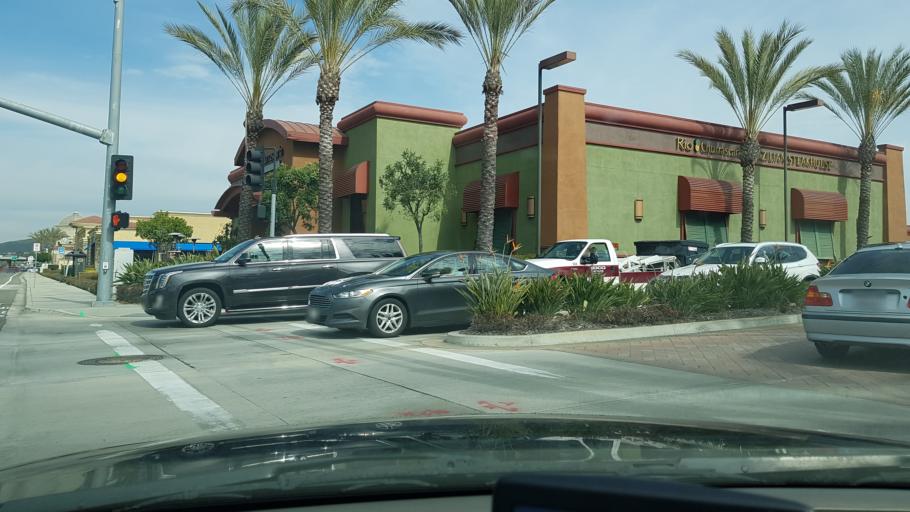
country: US
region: California
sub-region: San Diego County
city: Lake San Marcos
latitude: 33.1399
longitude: -117.1931
